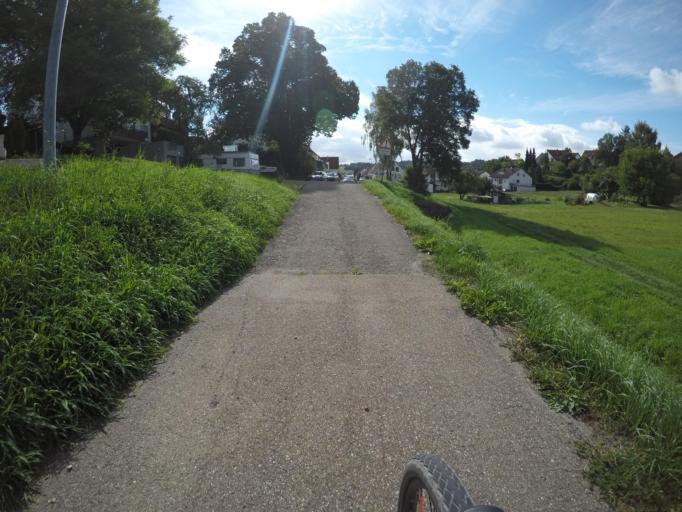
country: DE
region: Baden-Wuerttemberg
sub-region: Karlsruhe Region
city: Gechingen
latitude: 48.6986
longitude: 8.8249
